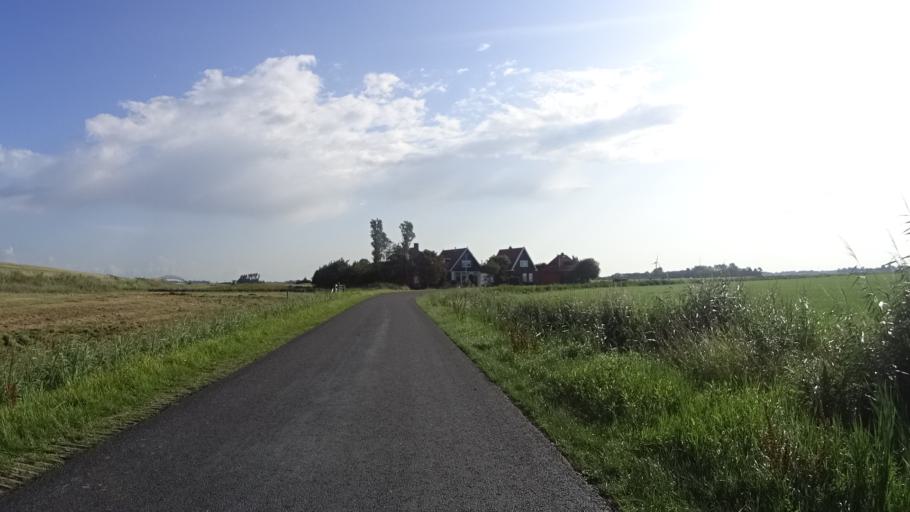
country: NL
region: Friesland
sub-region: Sudwest Fryslan
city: Makkum
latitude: 53.1145
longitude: 5.4005
